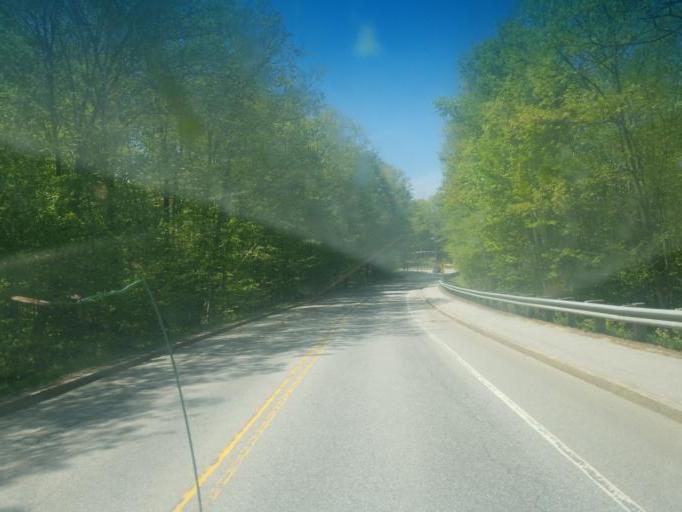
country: US
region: New Hampshire
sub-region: Grafton County
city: Plymouth
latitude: 43.7649
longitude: -71.7132
